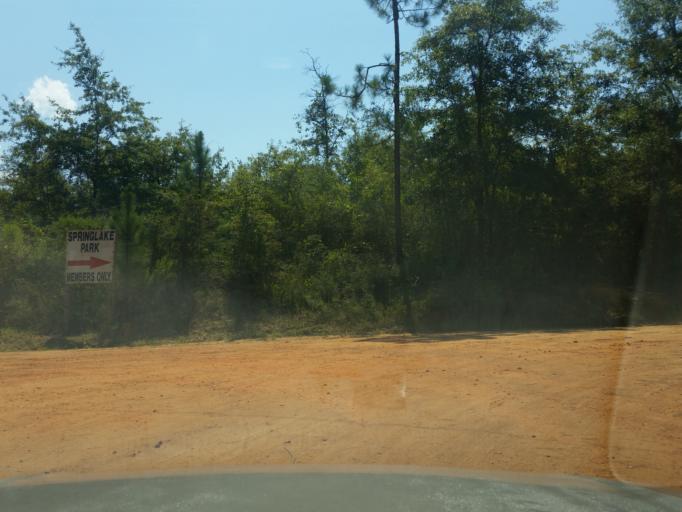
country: US
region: Florida
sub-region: Escambia County
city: Gonzalez
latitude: 30.6202
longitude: -87.2769
